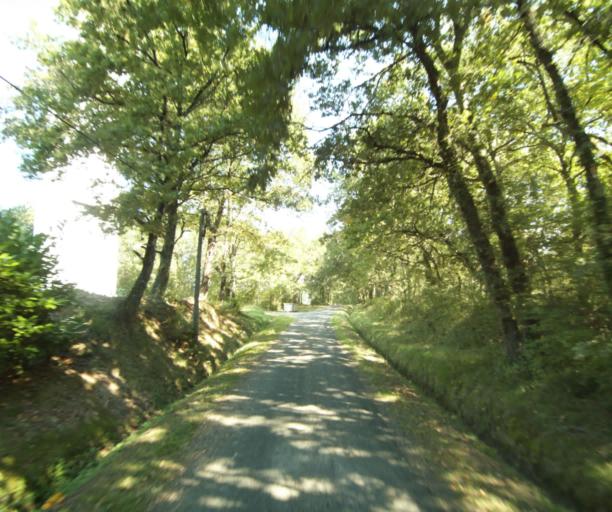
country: FR
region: Aquitaine
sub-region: Departement des Landes
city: Gabarret
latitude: 43.9542
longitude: -0.0211
